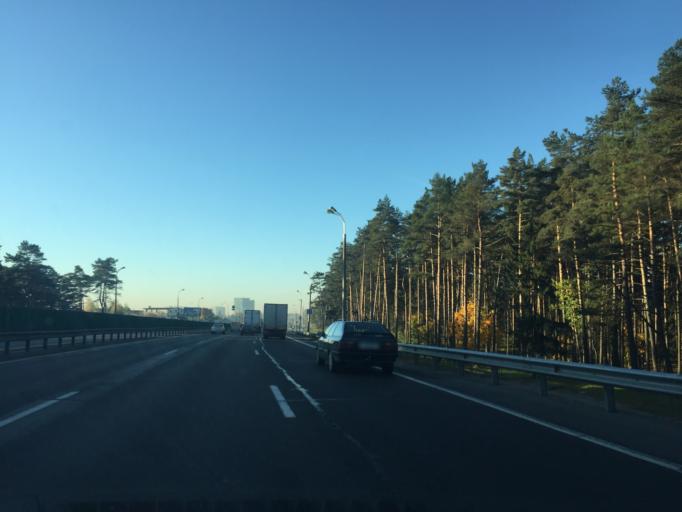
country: BY
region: Minsk
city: Vyaliki Trastsyanets
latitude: 53.8756
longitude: 27.6953
